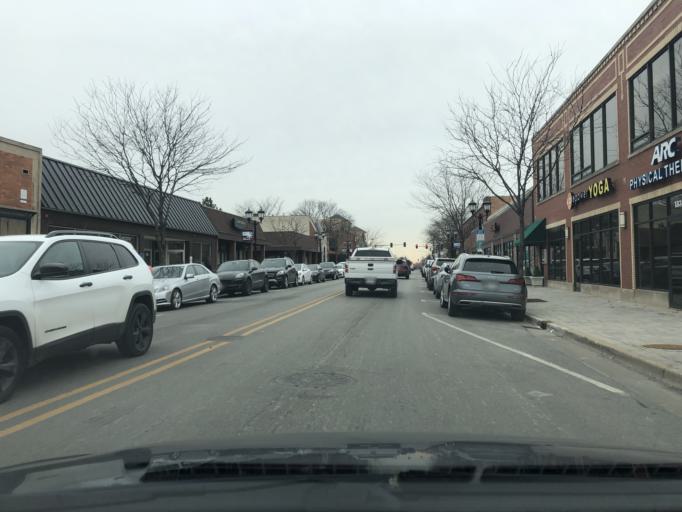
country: US
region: Illinois
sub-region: DuPage County
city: Elmhurst
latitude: 41.9023
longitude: -87.9398
